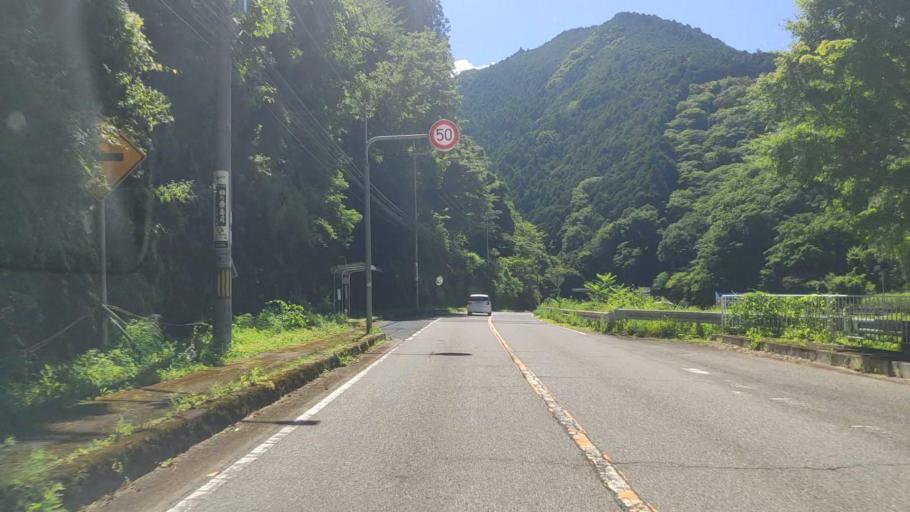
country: JP
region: Nara
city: Yoshino-cho
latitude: 34.3474
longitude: 135.9395
